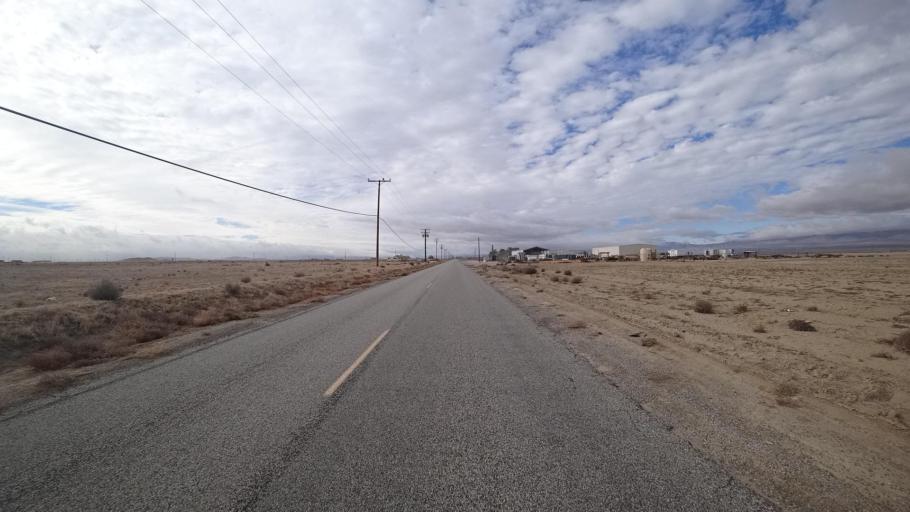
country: US
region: California
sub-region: Kern County
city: Rosamond
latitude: 34.8201
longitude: -118.2772
